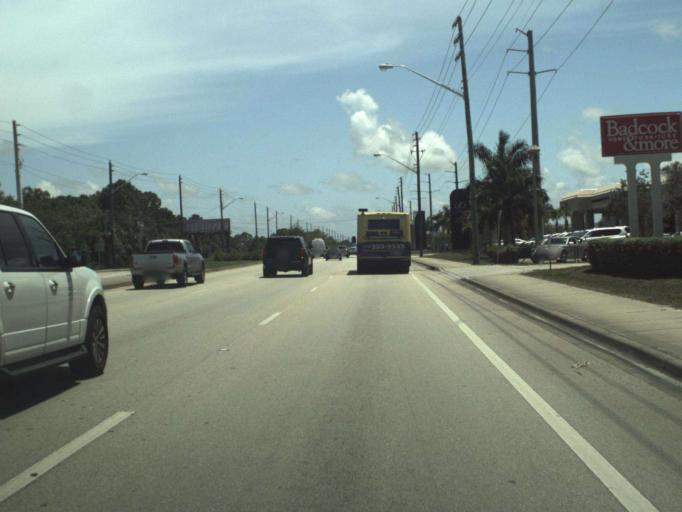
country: US
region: Florida
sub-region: Saint Lucie County
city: White City
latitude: 27.3732
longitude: -80.3260
